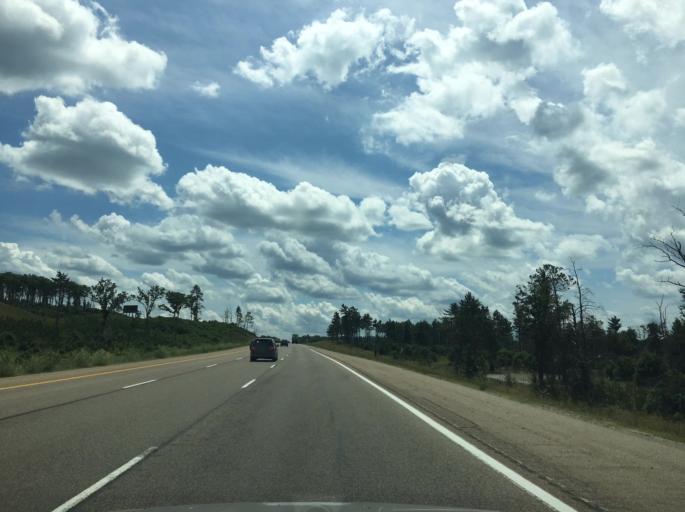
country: US
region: Michigan
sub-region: Crawford County
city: Grayling
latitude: 44.6403
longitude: -84.7089
